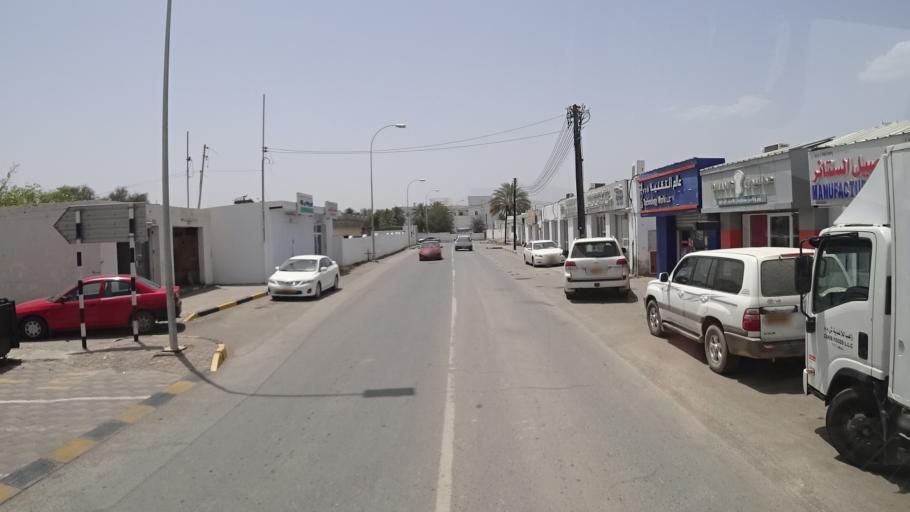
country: OM
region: Muhafazat Masqat
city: Muscat
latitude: 23.2590
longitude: 58.9141
